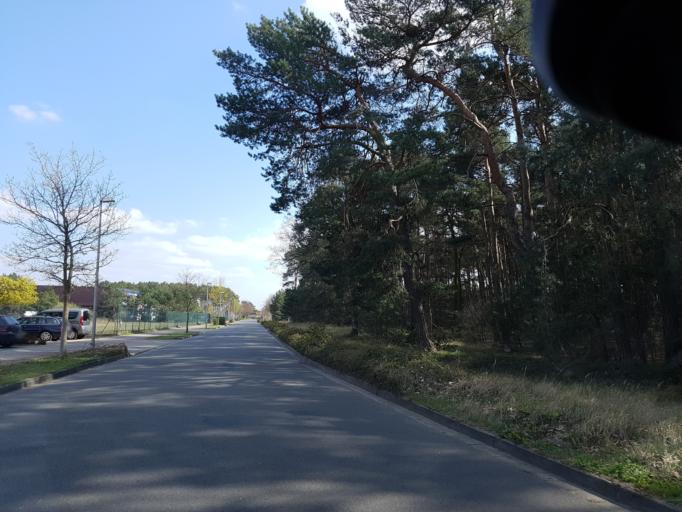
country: DE
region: Brandenburg
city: Linthe
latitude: 52.1641
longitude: 12.7797
